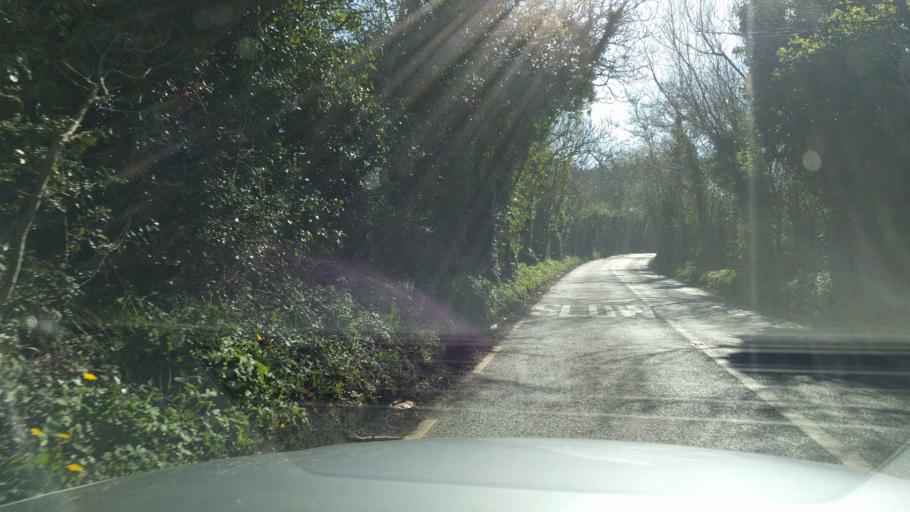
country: IE
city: Knocklyon
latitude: 53.2658
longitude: -6.3264
